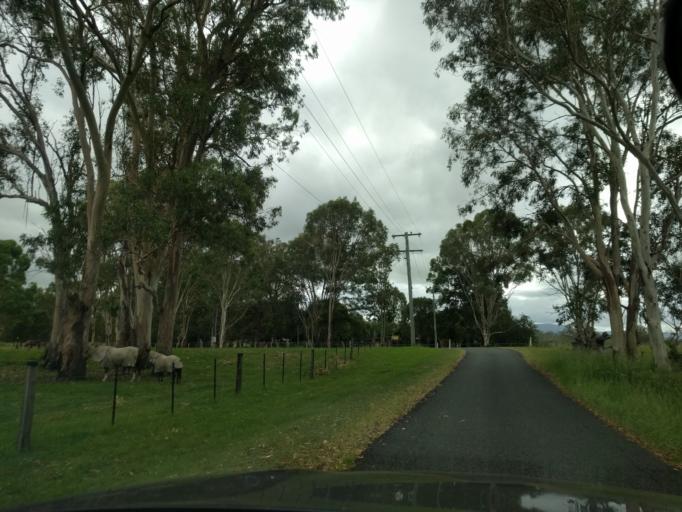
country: AU
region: Queensland
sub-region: Logan
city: Cedar Vale
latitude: -28.0221
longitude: 153.0050
